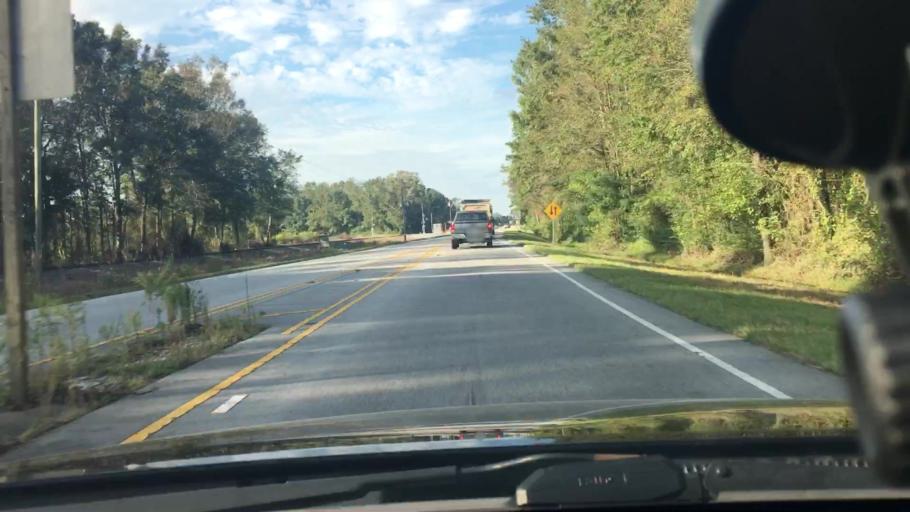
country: US
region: North Carolina
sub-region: Craven County
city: Vanceboro
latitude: 35.3367
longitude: -77.1512
